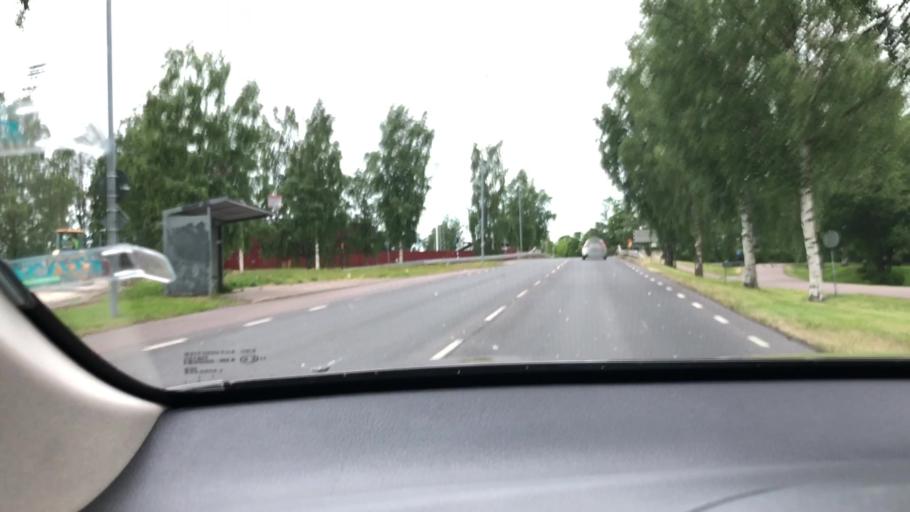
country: SE
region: Dalarna
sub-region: Borlange Kommun
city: Borlaenge
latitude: 60.4953
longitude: 15.4383
